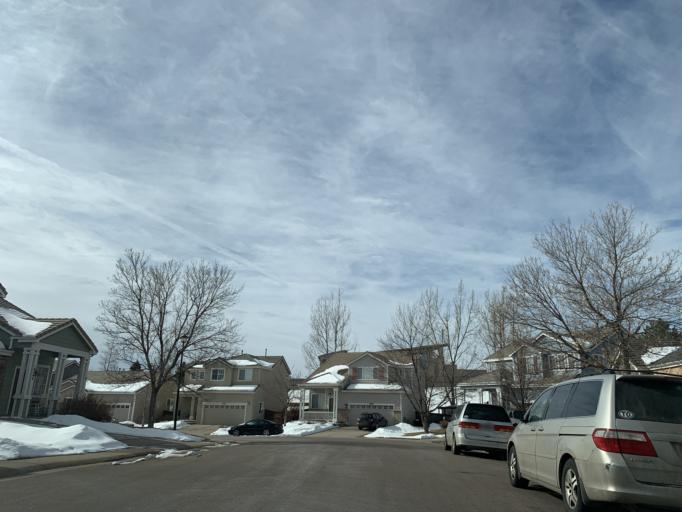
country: US
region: Colorado
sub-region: Douglas County
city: Carriage Club
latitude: 39.5249
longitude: -104.9330
